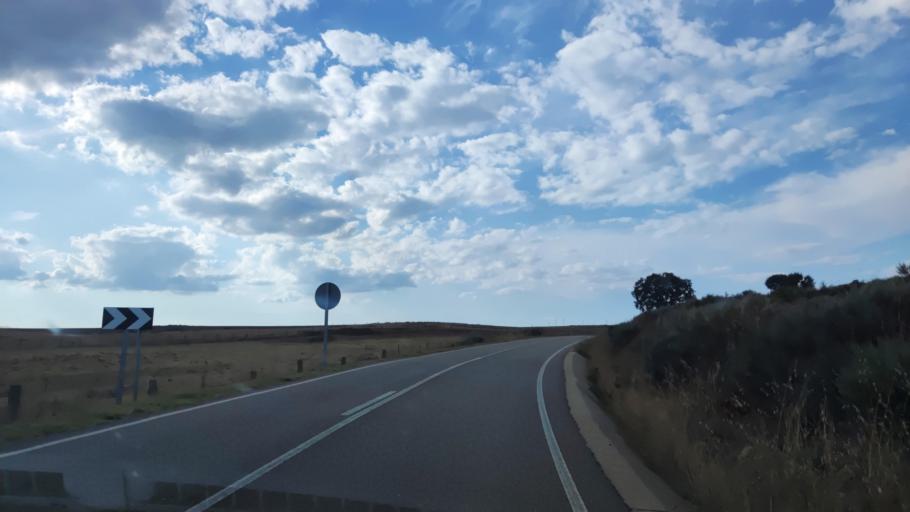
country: ES
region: Castille and Leon
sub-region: Provincia de Salamanca
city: Pastores
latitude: 40.5042
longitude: -6.5027
